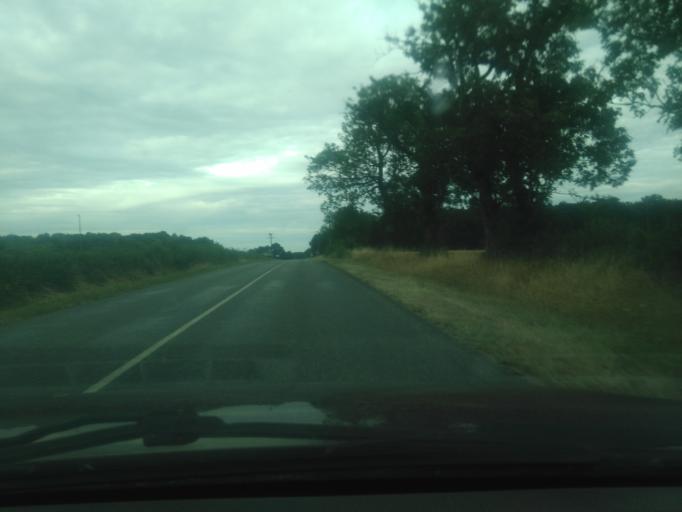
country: FR
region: Bourgogne
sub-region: Departement de la Nievre
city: Decize
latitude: 46.7908
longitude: 3.4373
